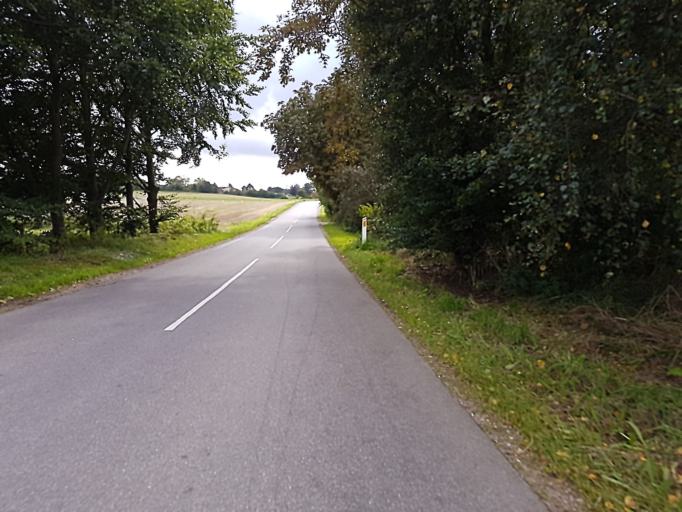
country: DK
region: Zealand
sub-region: Roskilde Kommune
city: Gundsomagle
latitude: 55.7210
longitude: 12.1372
